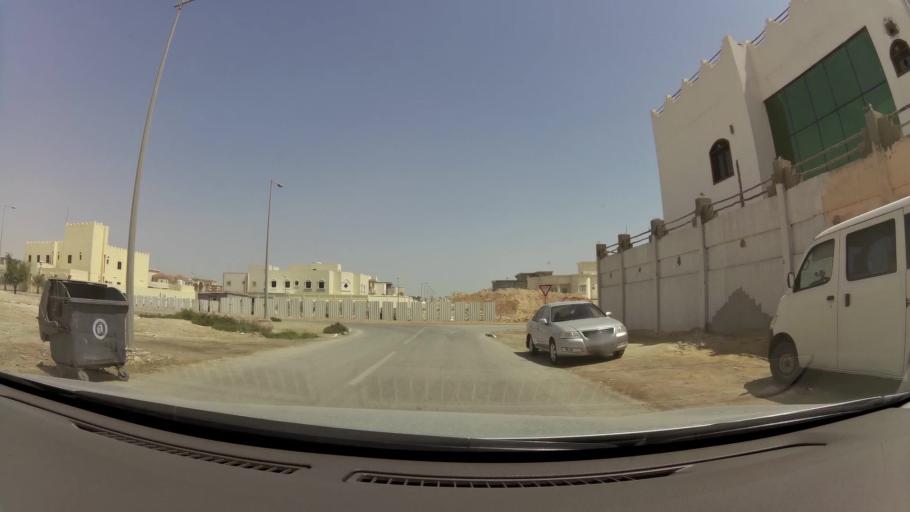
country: QA
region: Baladiyat Umm Salal
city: Umm Salal Muhammad
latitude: 25.4008
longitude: 51.4380
